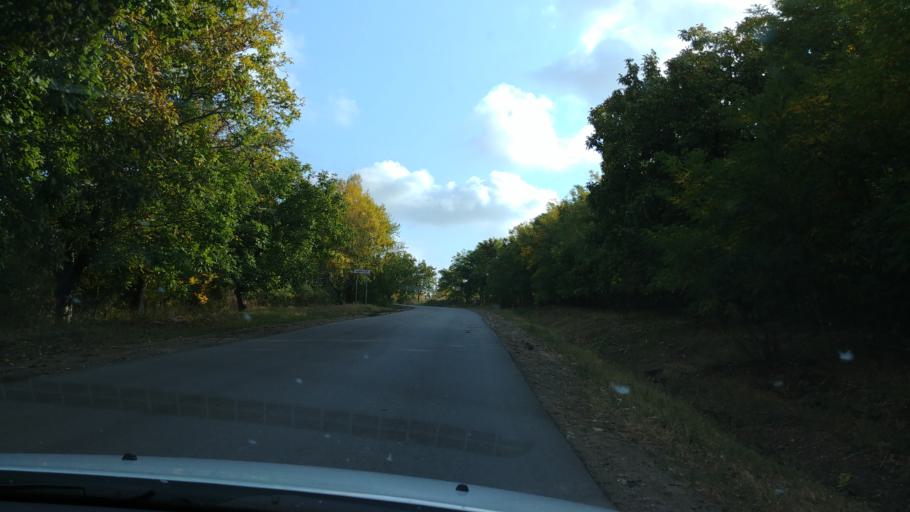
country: MD
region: Criuleni
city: Criuleni
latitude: 47.2165
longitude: 29.0669
